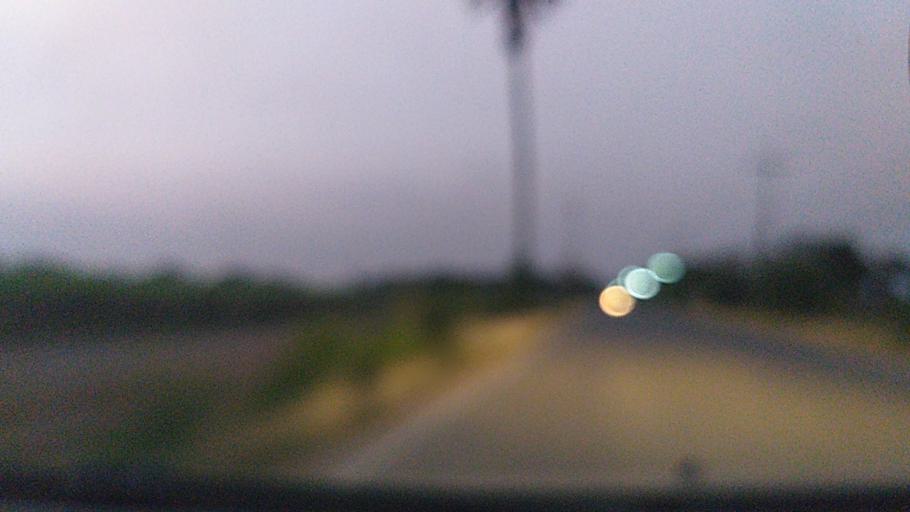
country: TH
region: Sing Buri
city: Sing Buri
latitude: 14.8406
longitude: 100.3934
